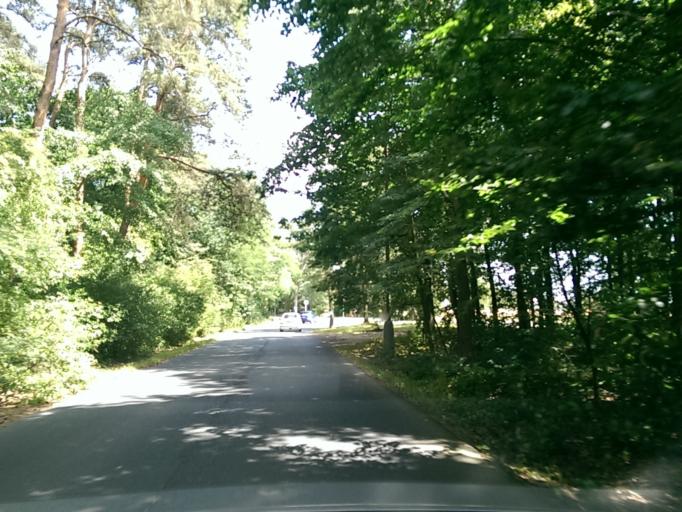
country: CZ
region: Central Bohemia
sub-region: Okres Melnik
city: Melnik
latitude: 50.3729
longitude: 14.5116
